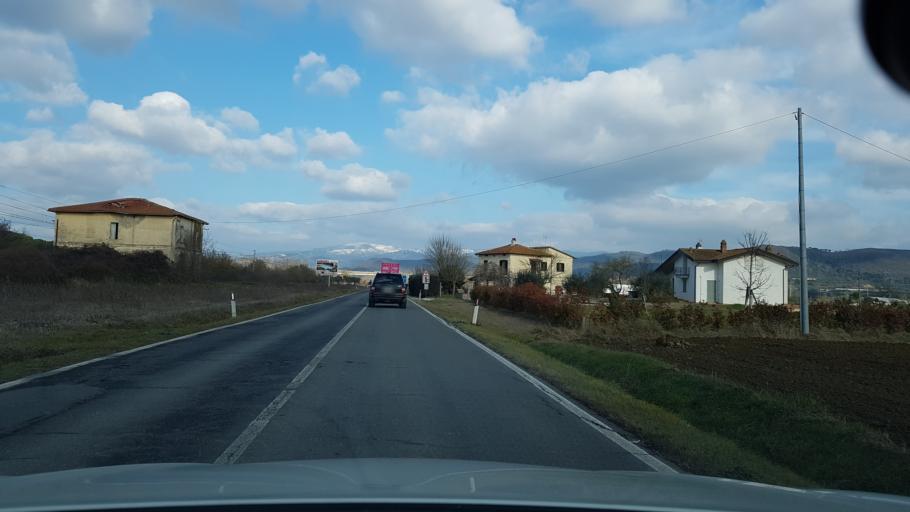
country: IT
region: Tuscany
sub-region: Province of Arezzo
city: Terontola
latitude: 43.1852
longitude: 12.0134
